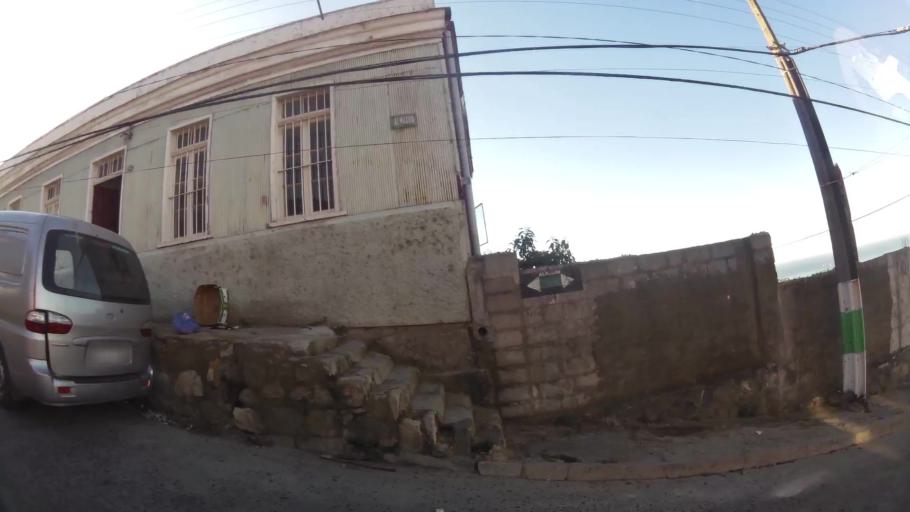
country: CL
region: Valparaiso
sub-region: Provincia de Valparaiso
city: Valparaiso
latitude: -33.0564
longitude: -71.6262
